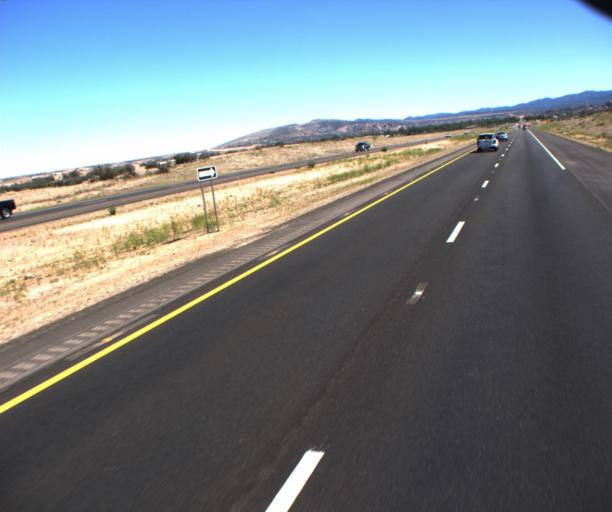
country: US
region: Arizona
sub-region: Yavapai County
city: Chino Valley
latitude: 34.6644
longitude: -112.4385
